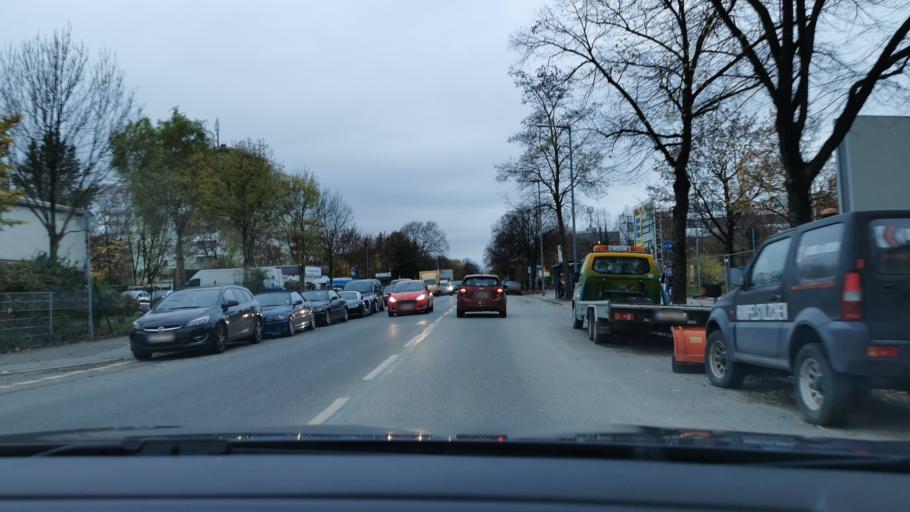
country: DE
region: Bavaria
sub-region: Upper Bavaria
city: Oberschleissheim
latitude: 48.2014
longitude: 11.5896
